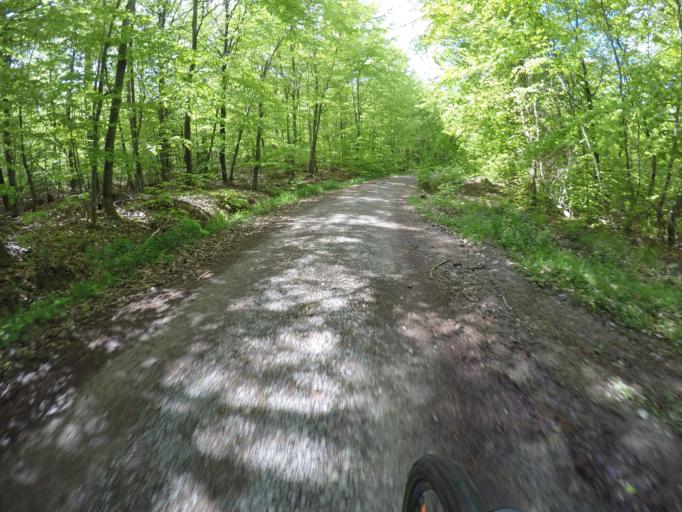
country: DE
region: Baden-Wuerttemberg
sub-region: Regierungsbezirk Stuttgart
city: Nufringen
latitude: 48.5950
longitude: 8.9244
